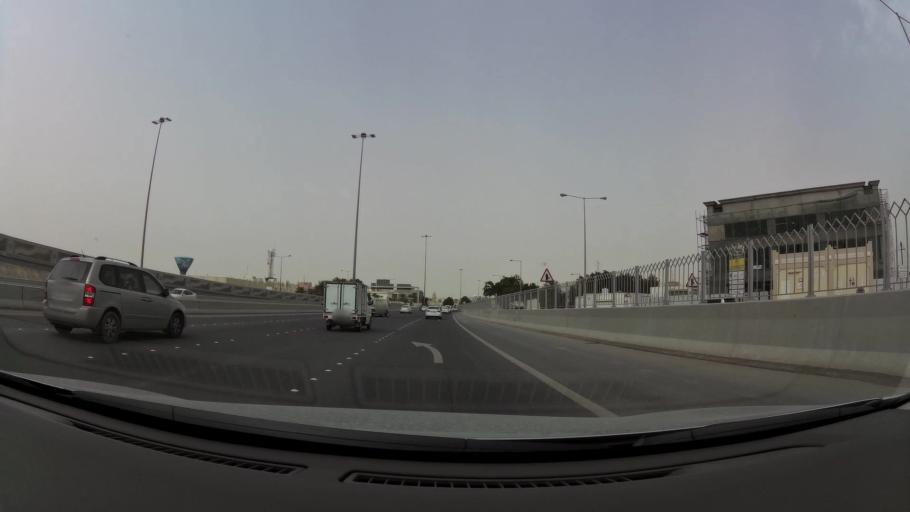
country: QA
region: Baladiyat ad Dawhah
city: Doha
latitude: 25.2563
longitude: 51.5043
